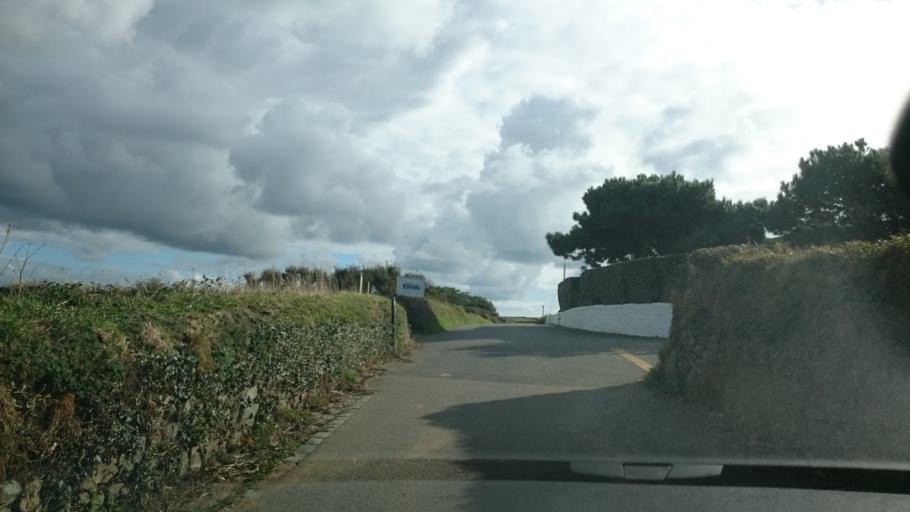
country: GG
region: St Peter Port
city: Saint Peter Port
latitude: 49.4295
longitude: -2.6642
